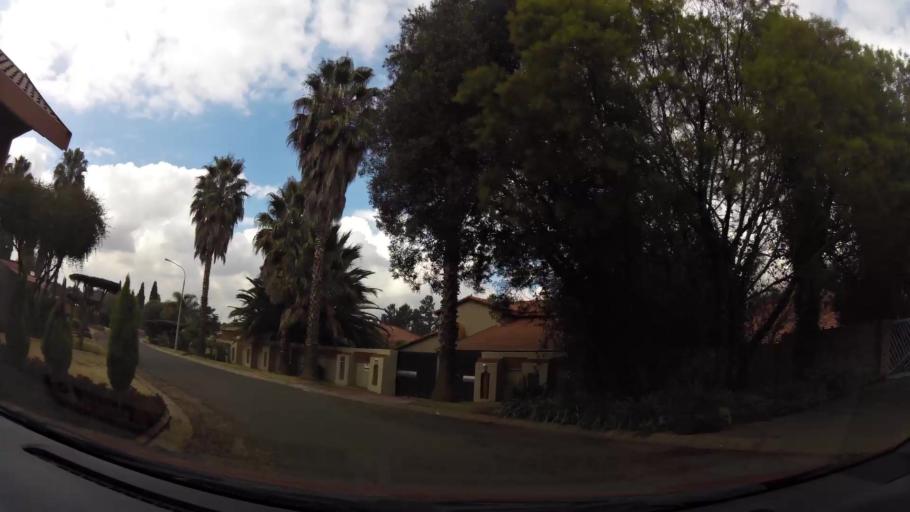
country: ZA
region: Gauteng
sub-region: Sedibeng District Municipality
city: Vanderbijlpark
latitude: -26.7418
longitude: 27.8500
